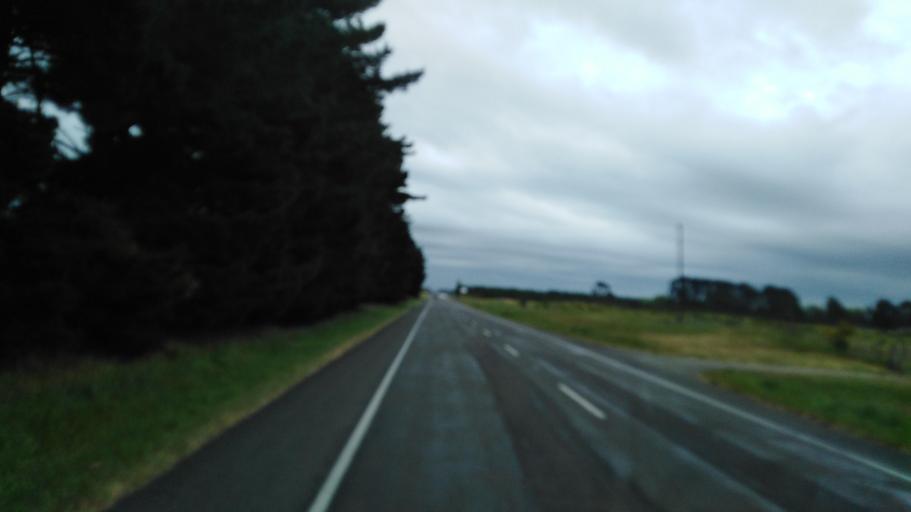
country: NZ
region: Manawatu-Wanganui
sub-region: Horowhenua District
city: Foxton
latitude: -40.4306
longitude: 175.3017
